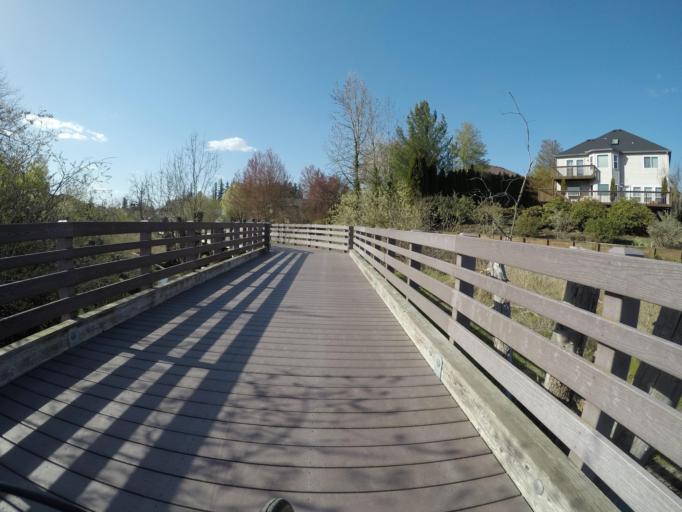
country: US
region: Oregon
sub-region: Washington County
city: Bethany
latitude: 45.5578
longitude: -122.8541
